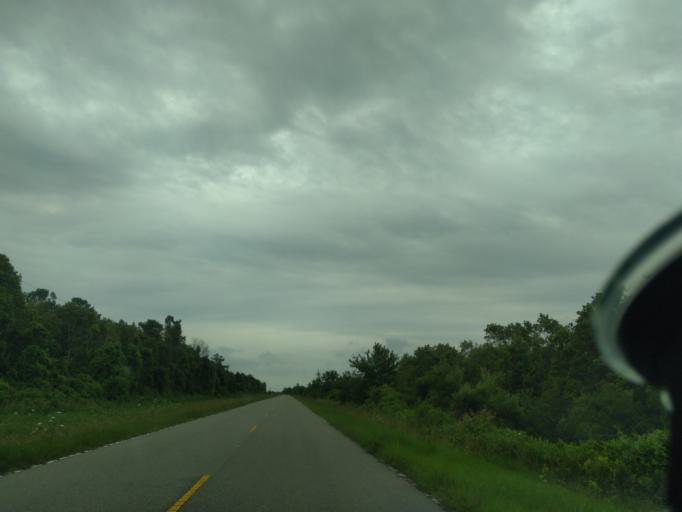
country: US
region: North Carolina
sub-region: Beaufort County
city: Belhaven
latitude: 35.7496
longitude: -76.5046
